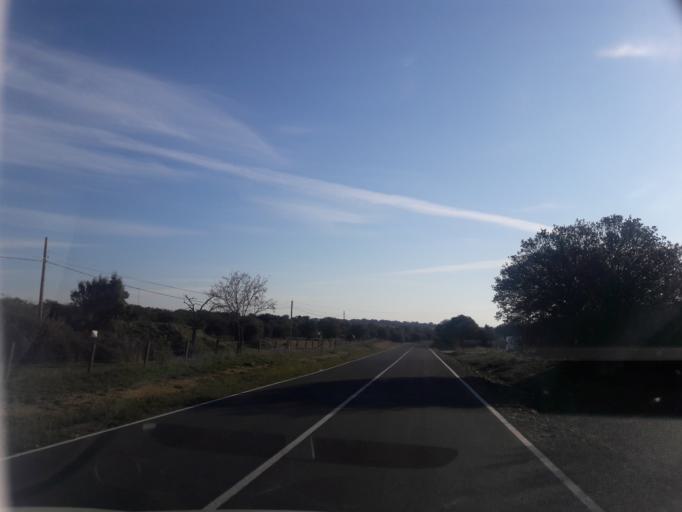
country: ES
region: Castille and Leon
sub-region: Provincia de Salamanca
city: Guijuelo
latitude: 40.5758
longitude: -5.6499
